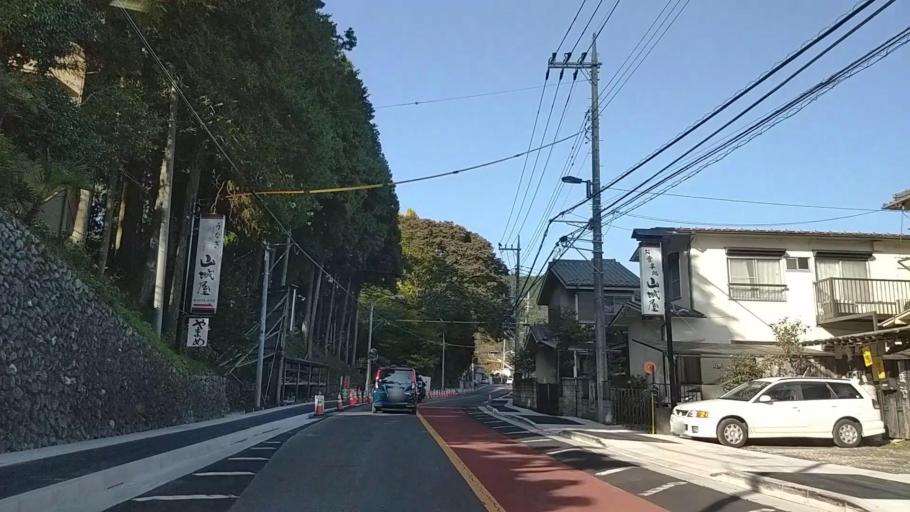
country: JP
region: Tokyo
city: Ome
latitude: 35.7855
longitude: 139.2363
